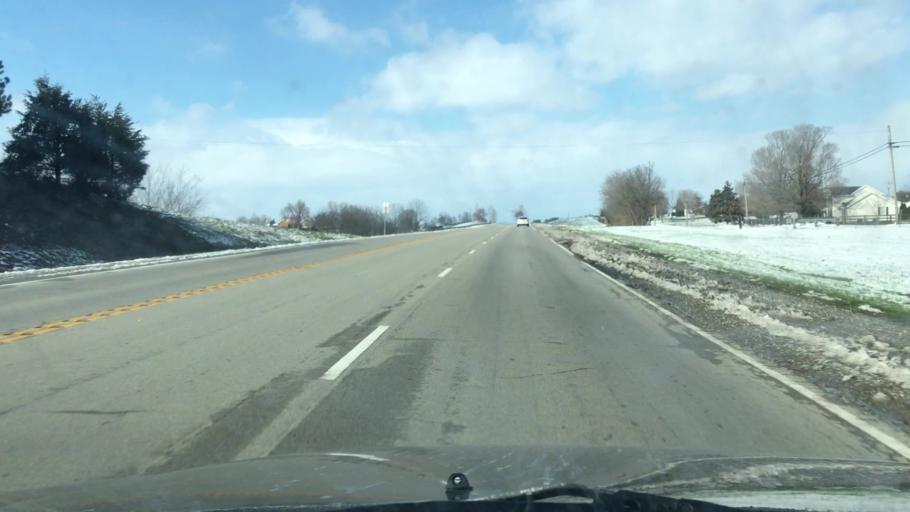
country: US
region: Kentucky
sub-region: Marion County
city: Lebanon
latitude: 37.5406
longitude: -85.3054
